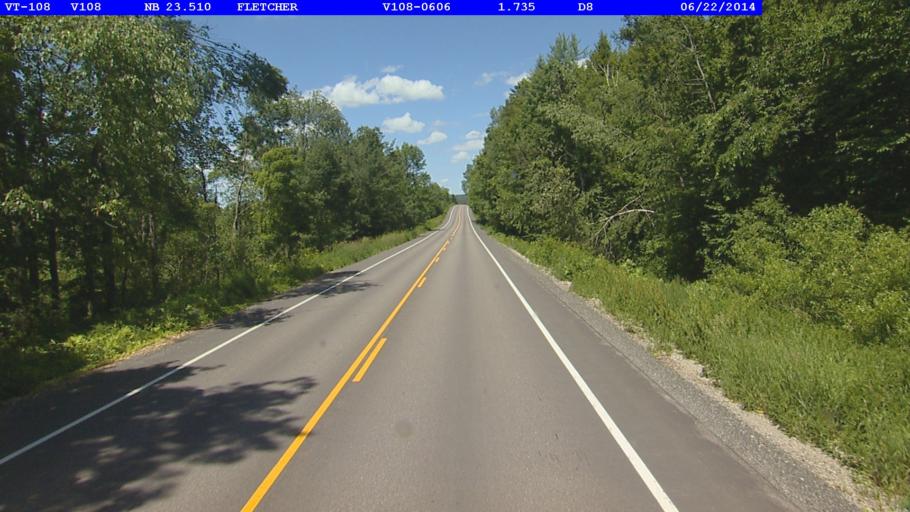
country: US
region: Vermont
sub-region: Lamoille County
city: Johnson
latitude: 44.7252
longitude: -72.8298
